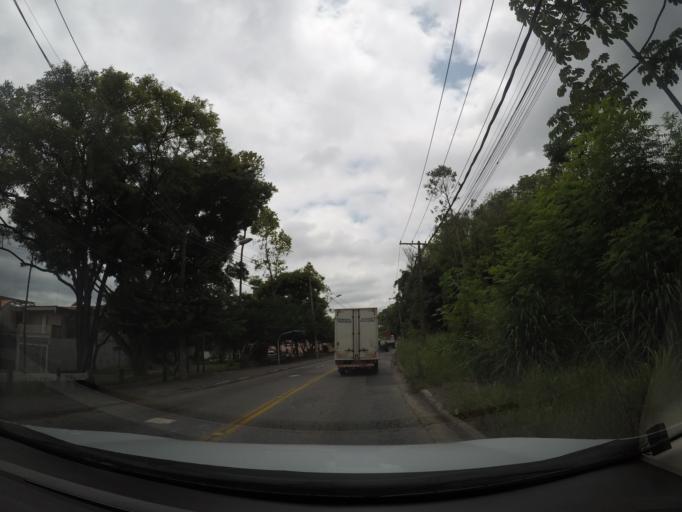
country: BR
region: Sao Paulo
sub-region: Itaquaquecetuba
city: Itaquaquecetuba
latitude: -23.4243
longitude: -46.4238
